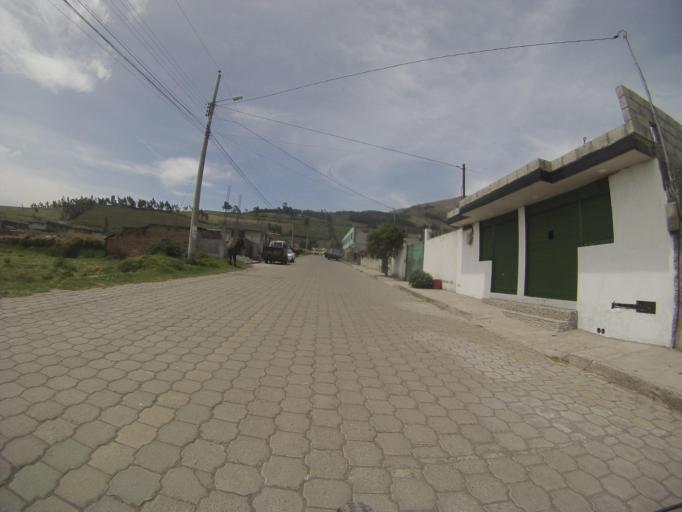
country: EC
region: Pichincha
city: Cayambe
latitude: 0.1566
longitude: -78.0700
